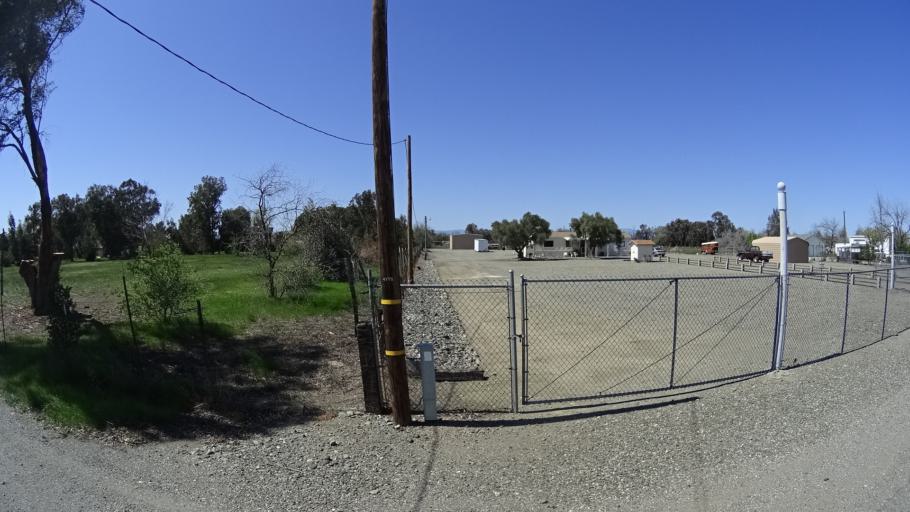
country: US
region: California
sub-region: Glenn County
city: Orland
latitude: 39.7791
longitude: -122.2386
